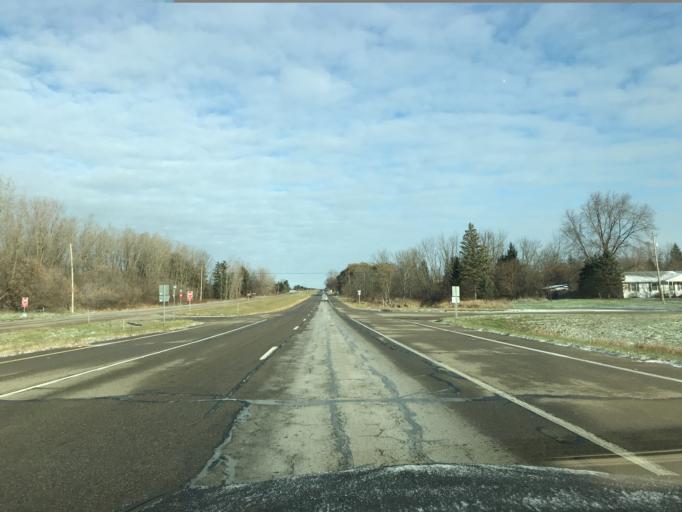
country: US
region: Michigan
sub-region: Eaton County
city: Dimondale
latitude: 42.5959
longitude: -84.6221
